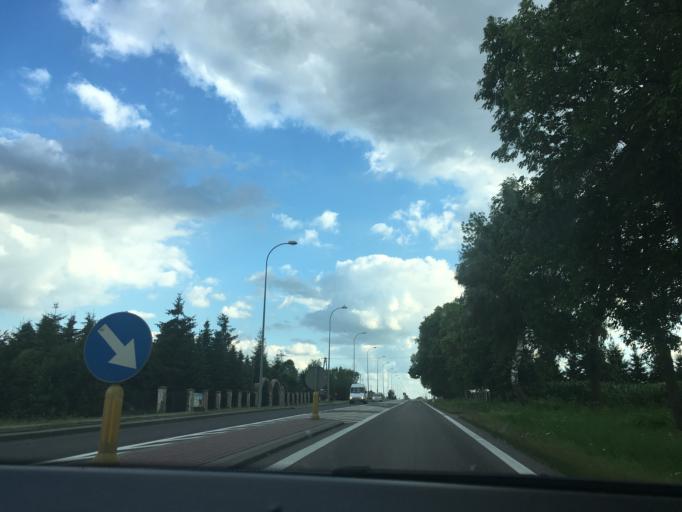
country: PL
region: Podlasie
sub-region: Powiat bielski
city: Bielsk Podlaski
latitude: 52.7874
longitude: 23.1883
